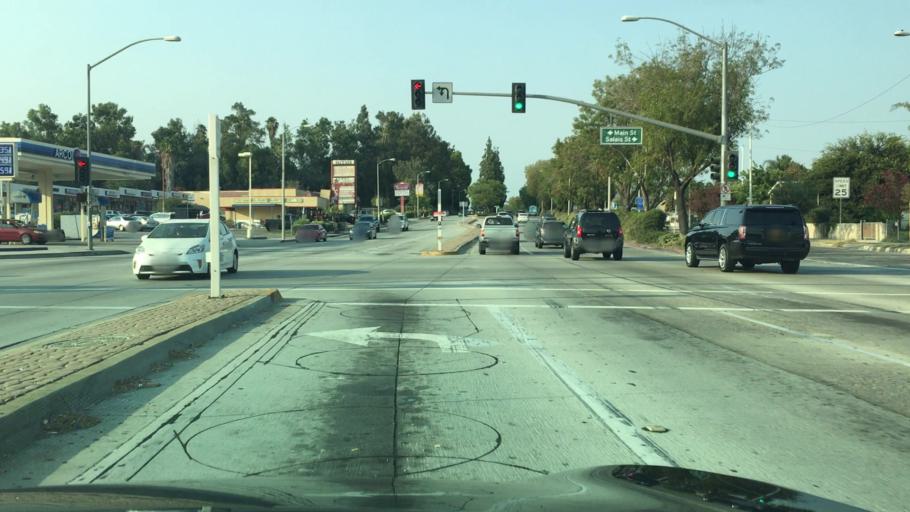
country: US
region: California
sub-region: Los Angeles County
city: South San Jose Hills
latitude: 34.0126
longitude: -117.9234
